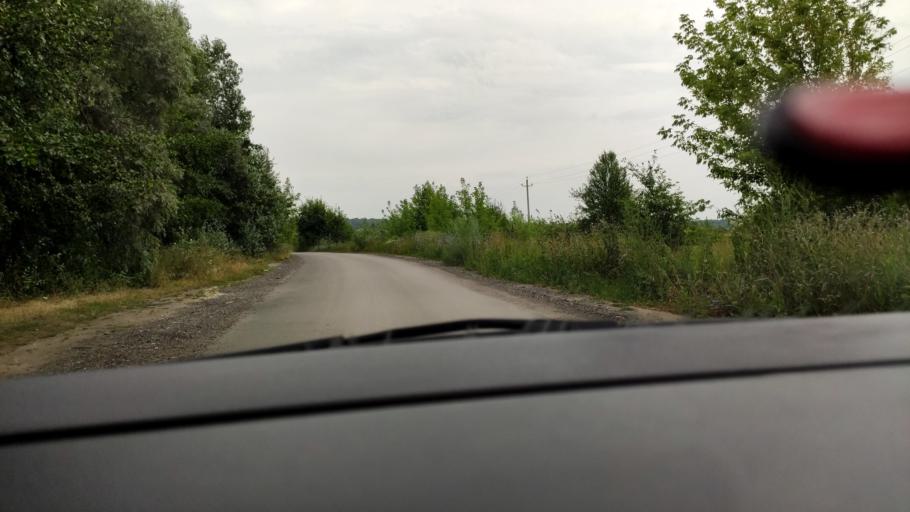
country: RU
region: Voronezj
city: Ramon'
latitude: 51.8956
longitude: 39.3515
